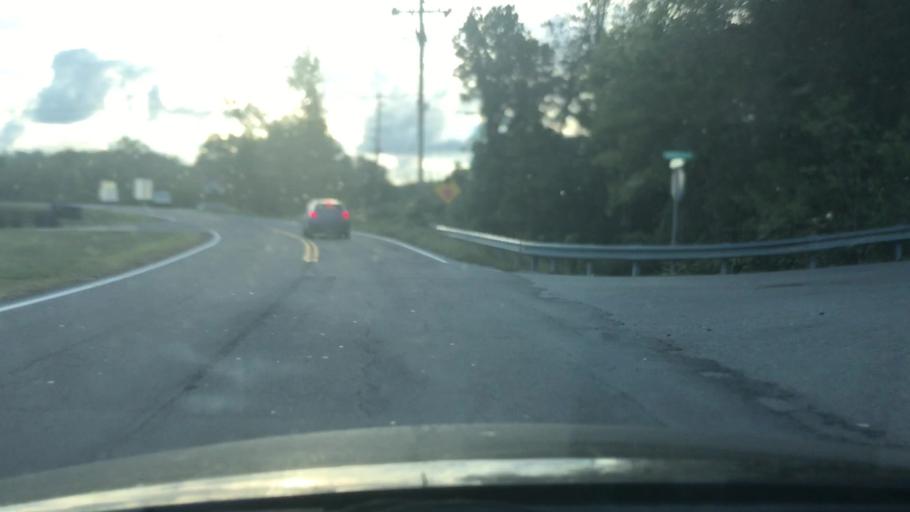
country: US
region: Tennessee
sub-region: Cheatham County
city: Ashland City
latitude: 36.2646
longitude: -87.0601
